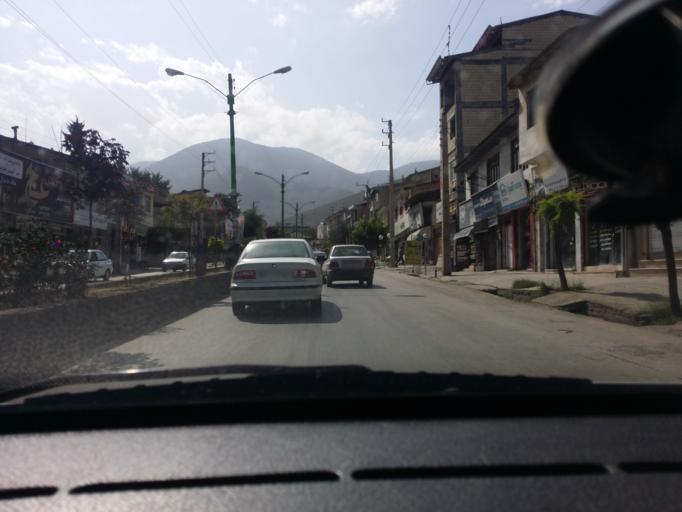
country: IR
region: Mazandaran
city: `Abbasabad
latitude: 36.5075
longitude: 51.1670
